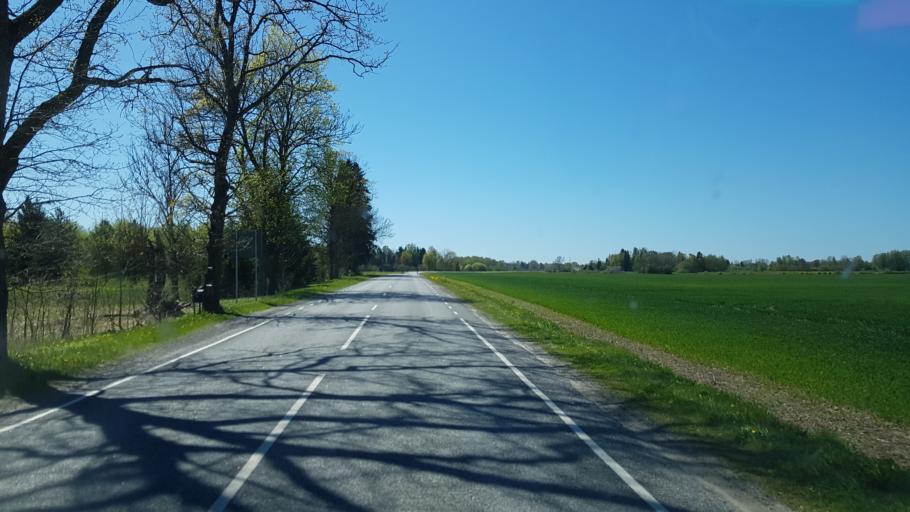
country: EE
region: Viljandimaa
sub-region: Vohma linn
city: Vohma
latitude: 58.6297
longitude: 25.6343
